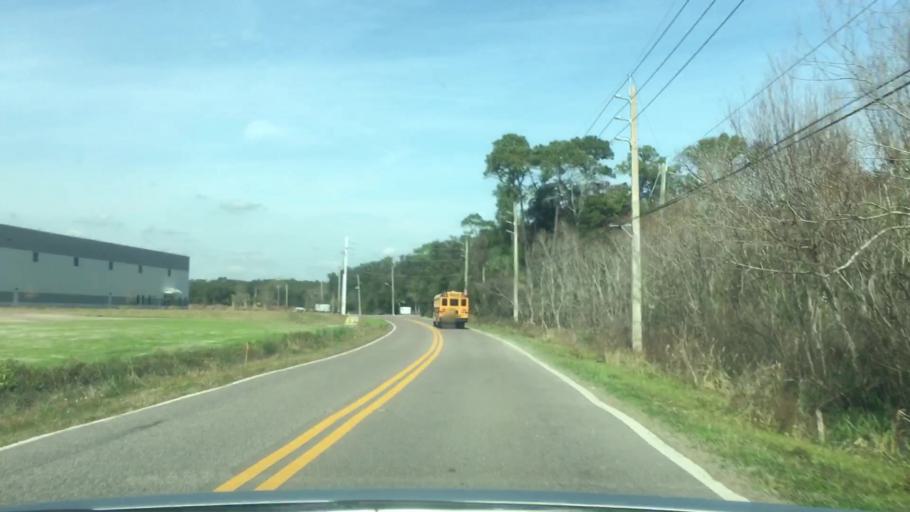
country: US
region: Florida
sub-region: Duval County
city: Jacksonville
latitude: 30.4553
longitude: -81.5582
